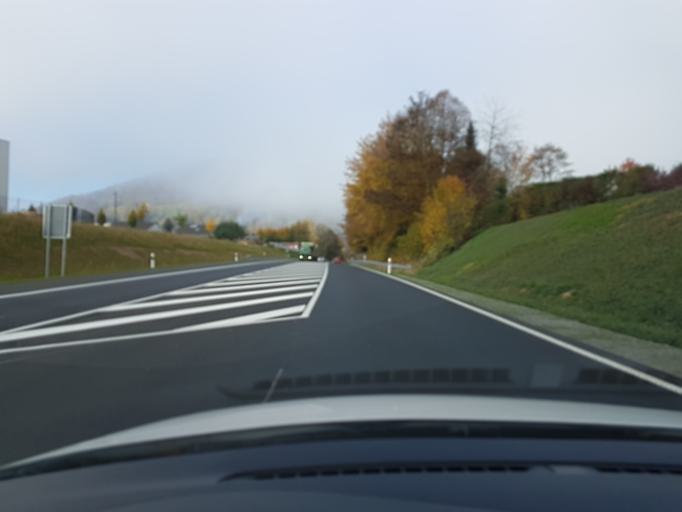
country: DE
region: Bavaria
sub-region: Regierungsbezirk Unterfranken
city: Kleinheubach
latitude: 49.7148
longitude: 9.2105
